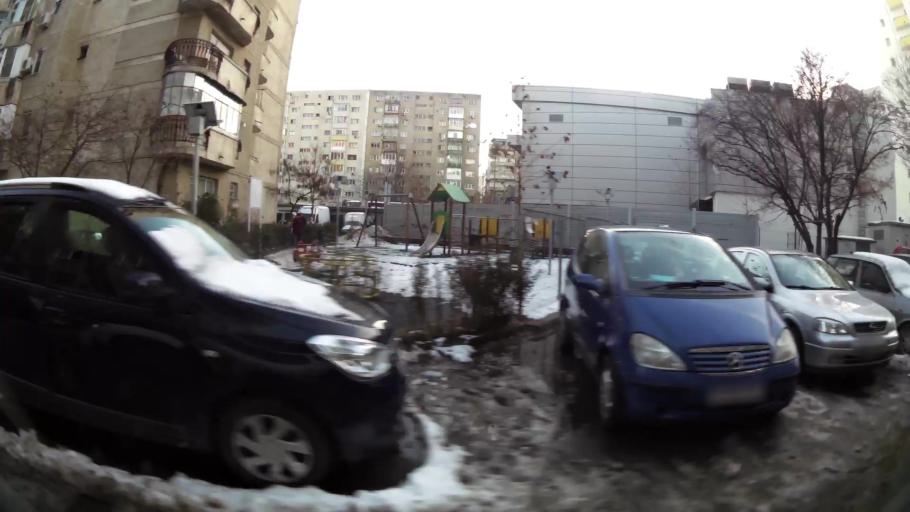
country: RO
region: Ilfov
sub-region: Comuna Fundeni-Dobroesti
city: Fundeni
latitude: 44.4452
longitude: 26.1443
